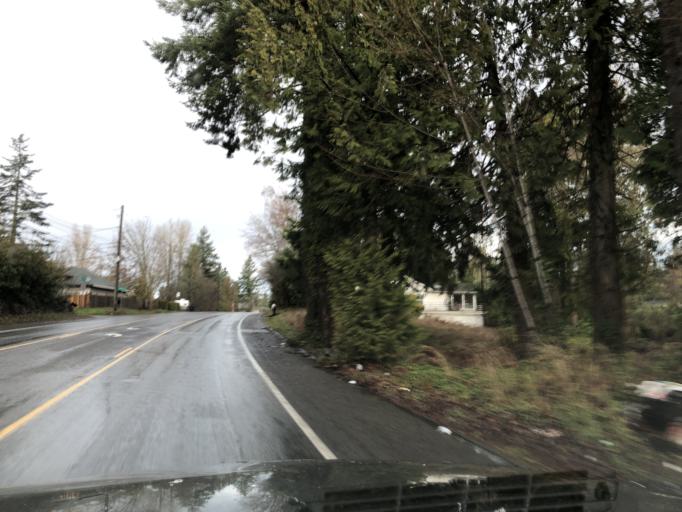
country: US
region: Washington
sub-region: Pierce County
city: Parkland
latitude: 47.1623
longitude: -122.4410
